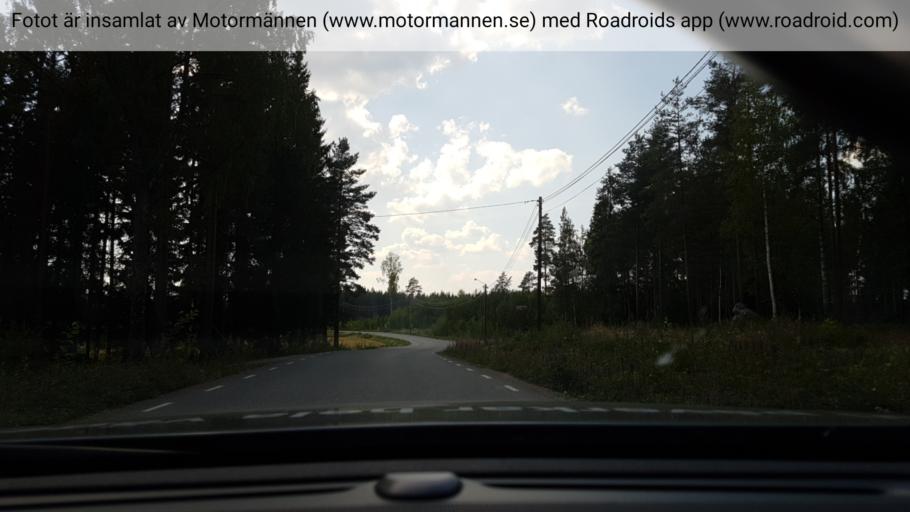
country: SE
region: Dalarna
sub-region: Faluns Kommun
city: Svardsjo
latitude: 60.7237
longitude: 15.8140
